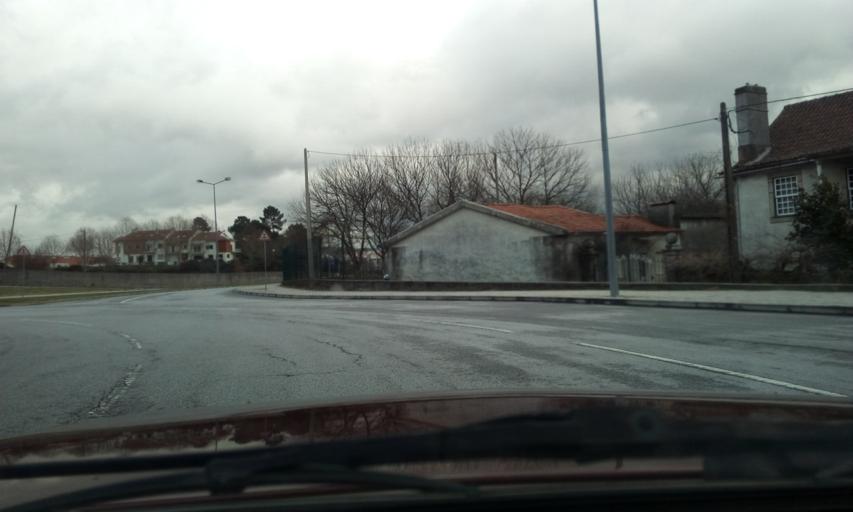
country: PT
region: Viseu
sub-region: Viseu
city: Viseu
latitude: 40.6681
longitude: -7.8974
